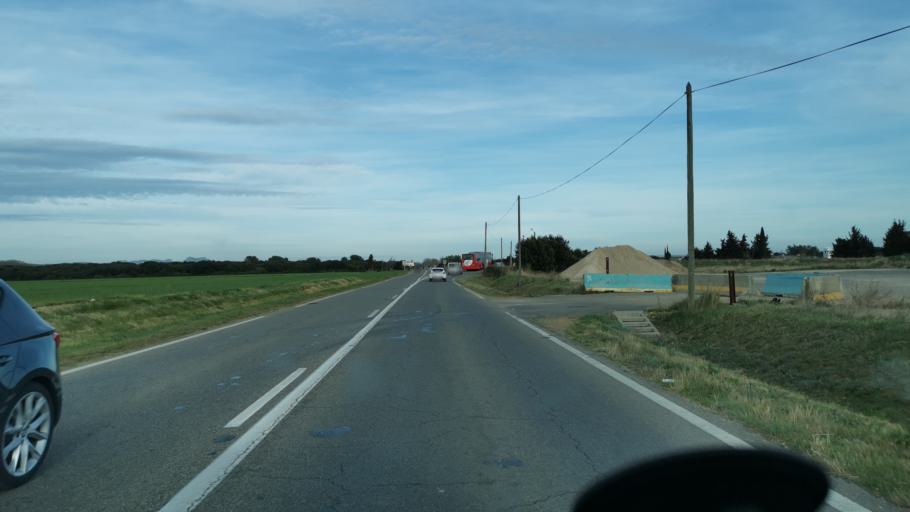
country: FR
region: Provence-Alpes-Cote d'Azur
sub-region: Departement des Bouches-du-Rhone
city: Saint-Martin-de-Crau
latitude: 43.6346
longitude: 4.7747
